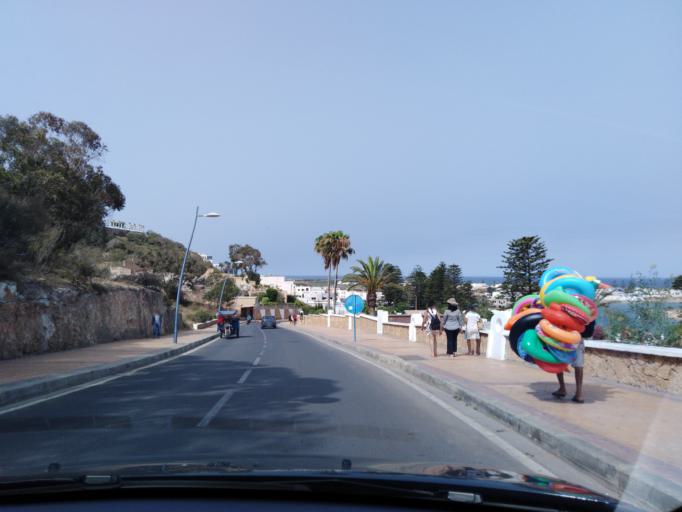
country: MA
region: Doukkala-Abda
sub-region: Safi
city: Safi
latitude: 32.7343
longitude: -9.0357
